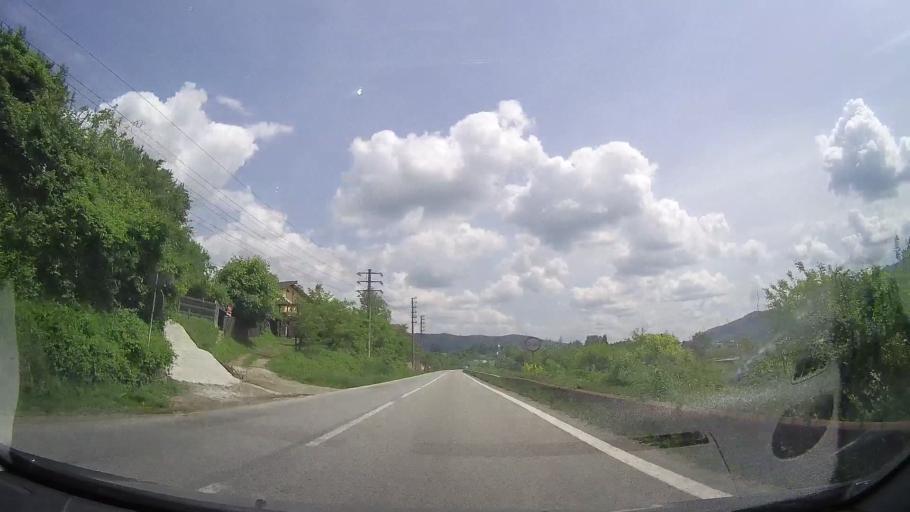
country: RO
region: Valcea
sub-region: Oras Calimanesti
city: Jiblea Veche
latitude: 45.2471
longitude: 24.3449
